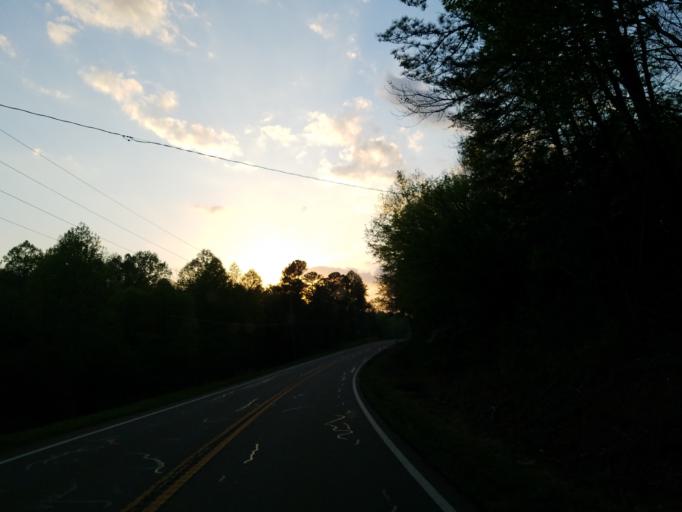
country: US
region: Georgia
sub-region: Pickens County
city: Jasper
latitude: 34.5130
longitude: -84.4532
